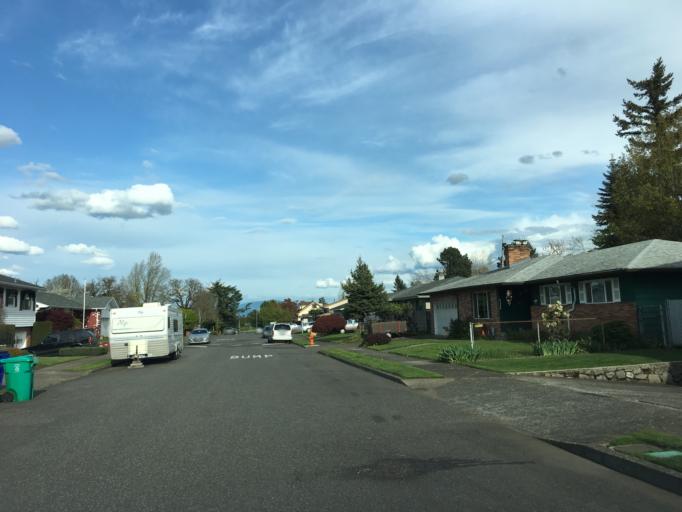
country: US
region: Oregon
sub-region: Multnomah County
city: Lents
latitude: 45.5452
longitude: -122.5407
